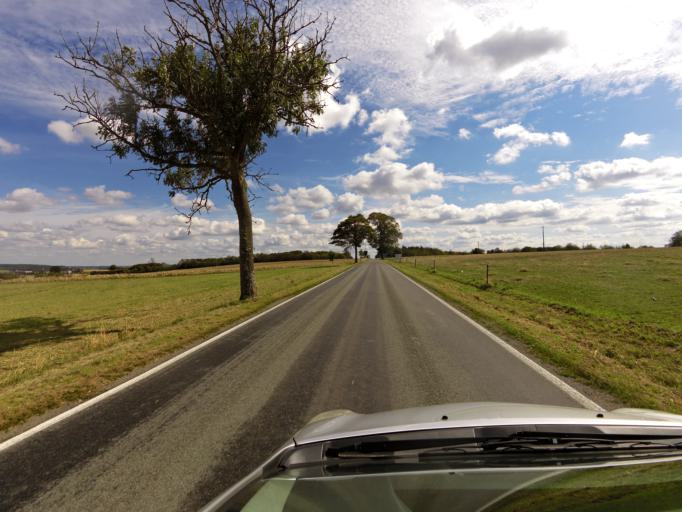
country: BE
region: Wallonia
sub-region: Province de Namur
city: Somme-Leuze
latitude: 50.3538
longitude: 5.3364
